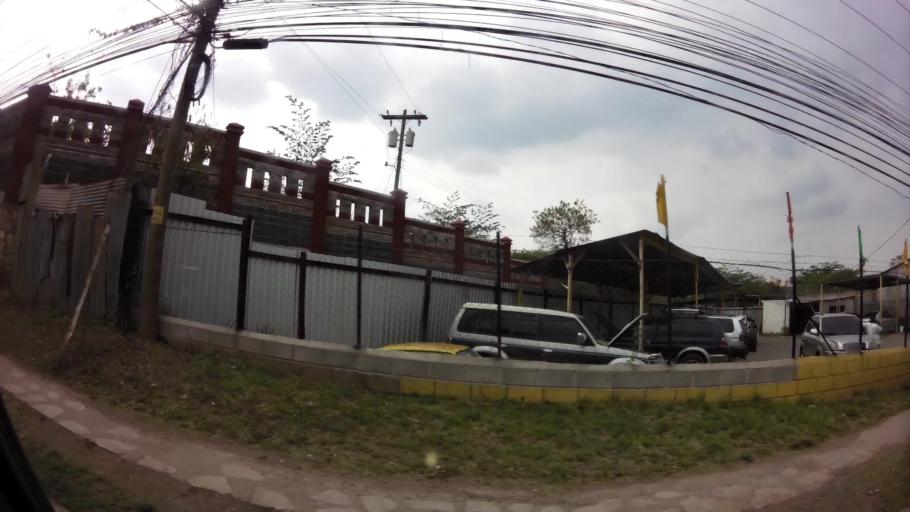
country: HN
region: Francisco Morazan
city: Tegucigalpa
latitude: 14.0913
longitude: -87.1713
